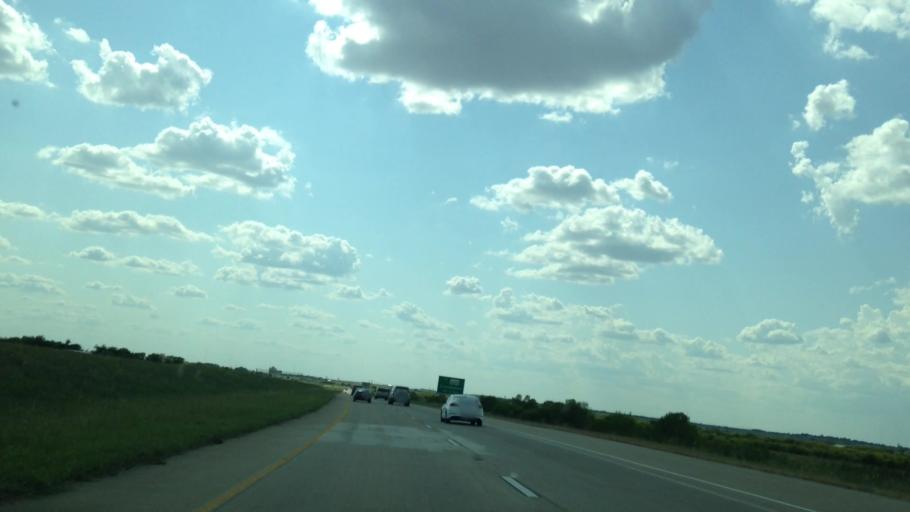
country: US
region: Texas
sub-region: Travis County
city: Onion Creek
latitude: 30.0826
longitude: -97.7115
